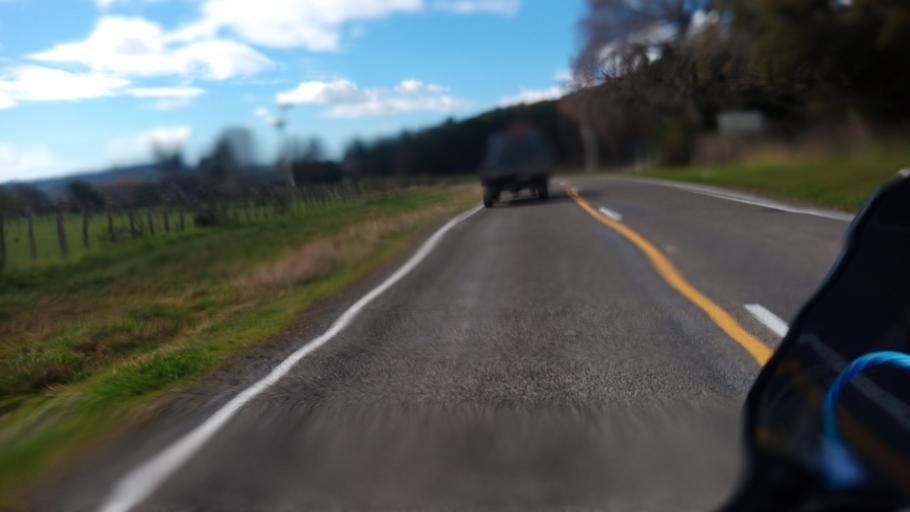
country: NZ
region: Gisborne
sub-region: Gisborne District
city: Gisborne
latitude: -37.9066
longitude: 178.2912
